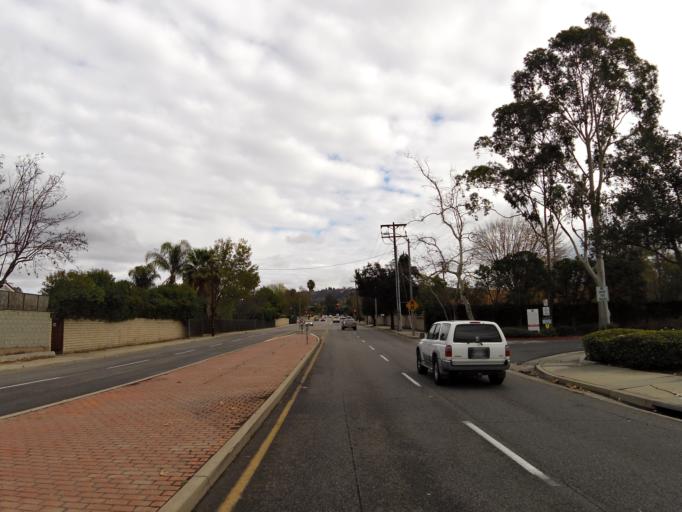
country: US
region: California
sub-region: Ventura County
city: Thousand Oaks
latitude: 34.1996
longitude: -118.8661
